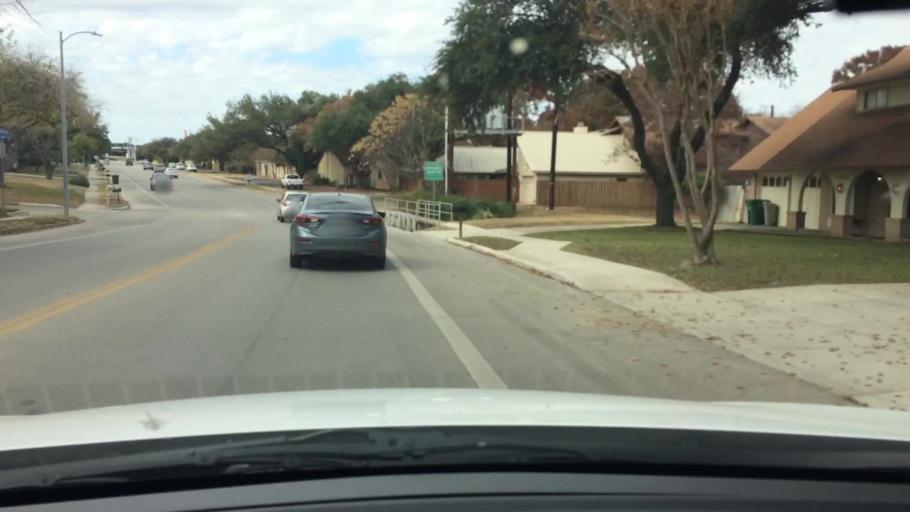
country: US
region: Texas
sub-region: Bexar County
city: Hollywood Park
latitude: 29.5769
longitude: -98.4703
